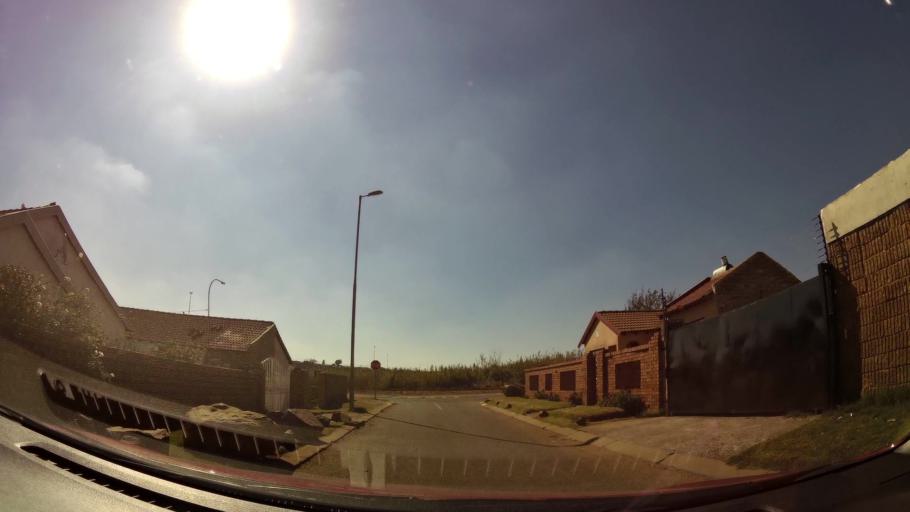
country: ZA
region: Gauteng
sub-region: City of Johannesburg Metropolitan Municipality
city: Soweto
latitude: -26.2343
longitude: 27.8202
